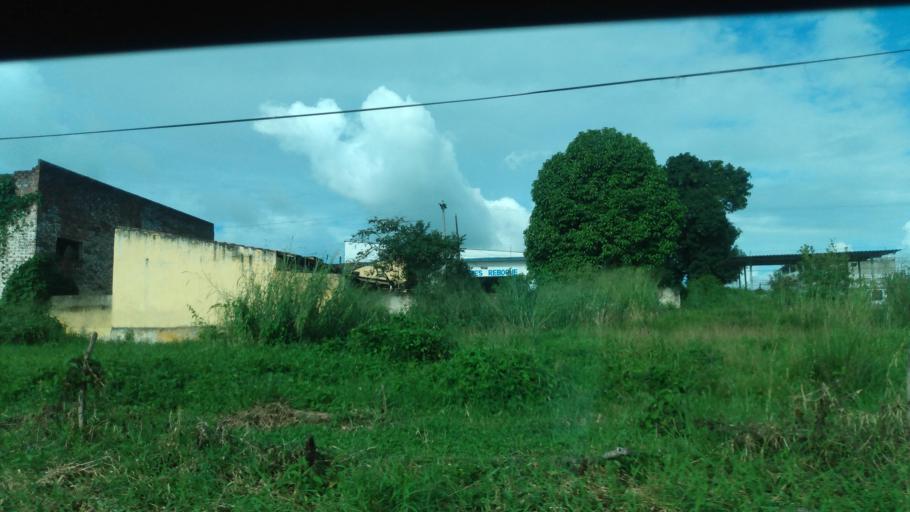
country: BR
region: Pernambuco
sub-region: Palmares
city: Palmares
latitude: -8.6767
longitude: -35.5794
